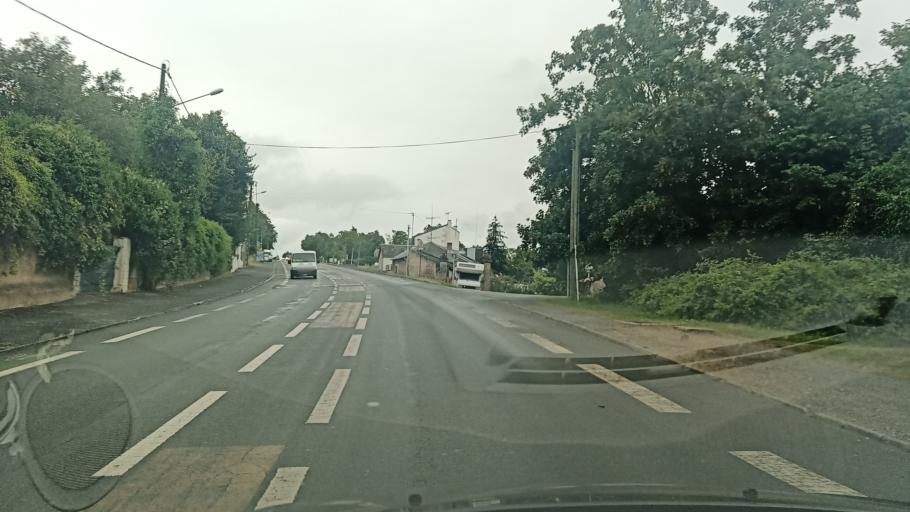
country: FR
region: Poitou-Charentes
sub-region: Departement de la Vienne
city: Poitiers
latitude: 46.6085
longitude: 0.3473
